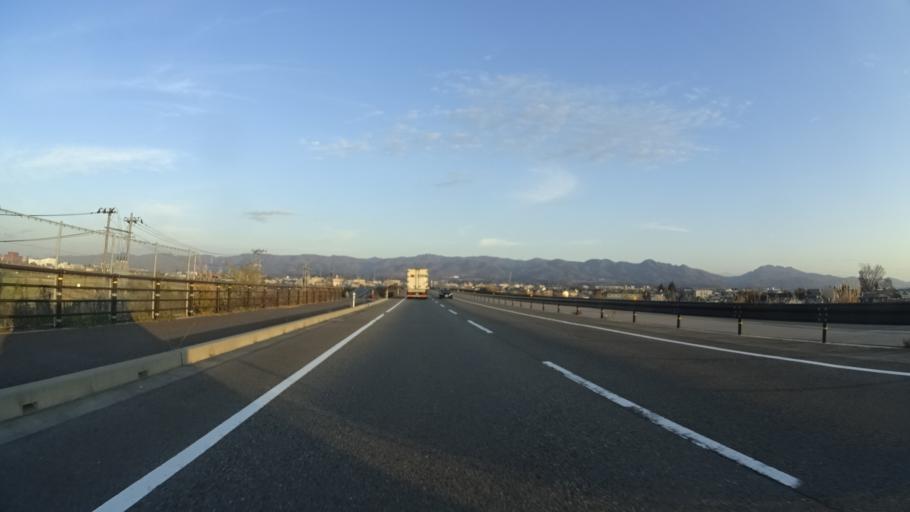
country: JP
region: Niigata
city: Nagaoka
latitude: 37.4295
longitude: 138.8271
